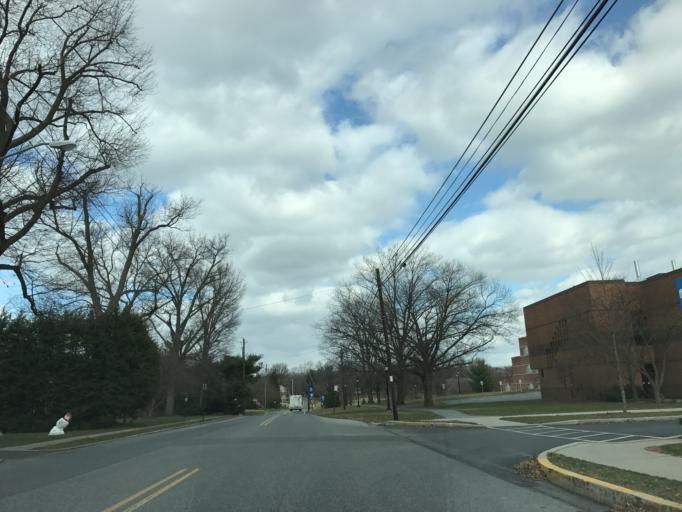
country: US
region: Pennsylvania
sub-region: Lancaster County
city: Elizabethtown
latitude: 40.1514
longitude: -76.5931
